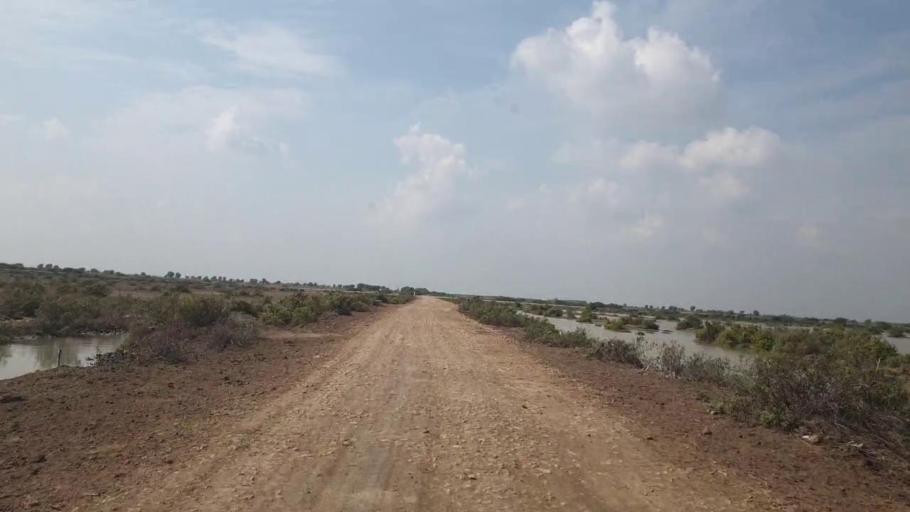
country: PK
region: Sindh
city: Badin
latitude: 24.5066
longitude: 68.6105
